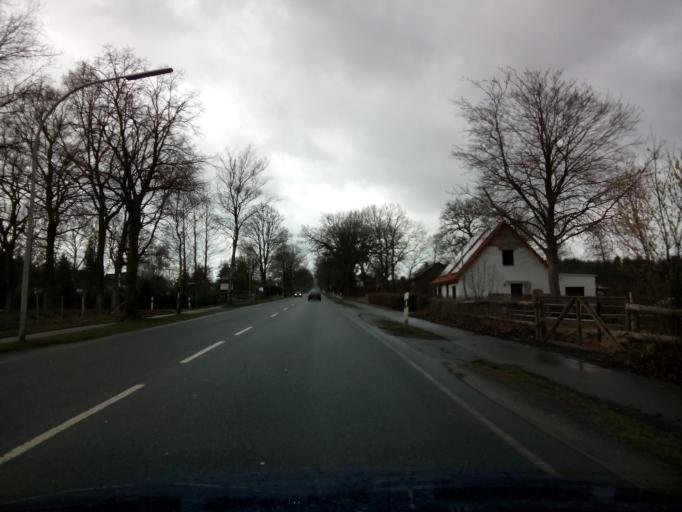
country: DE
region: Lower Saxony
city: Osterholz-Scharmbeck
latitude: 53.2121
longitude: 8.7724
